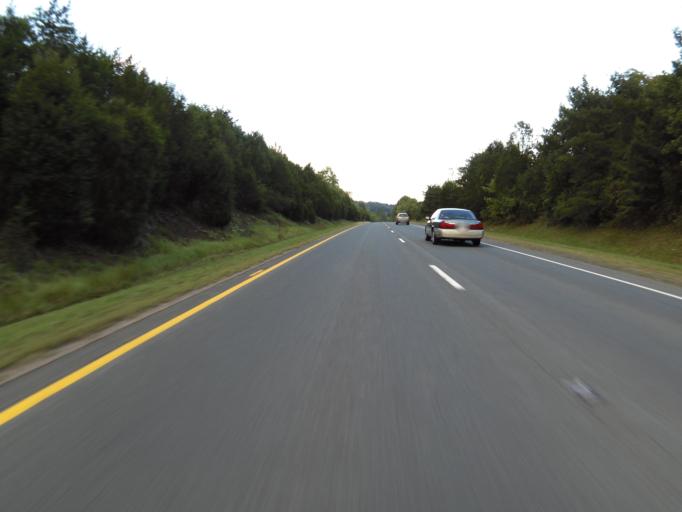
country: US
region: Virginia
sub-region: Fauquier County
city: Warrenton
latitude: 38.6941
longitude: -77.8927
